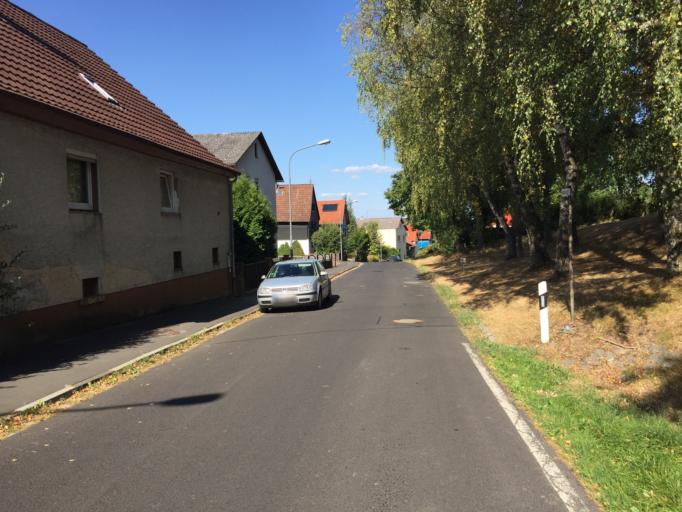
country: DE
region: Hesse
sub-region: Regierungsbezirk Giessen
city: Grunberg
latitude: 50.6171
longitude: 8.9347
